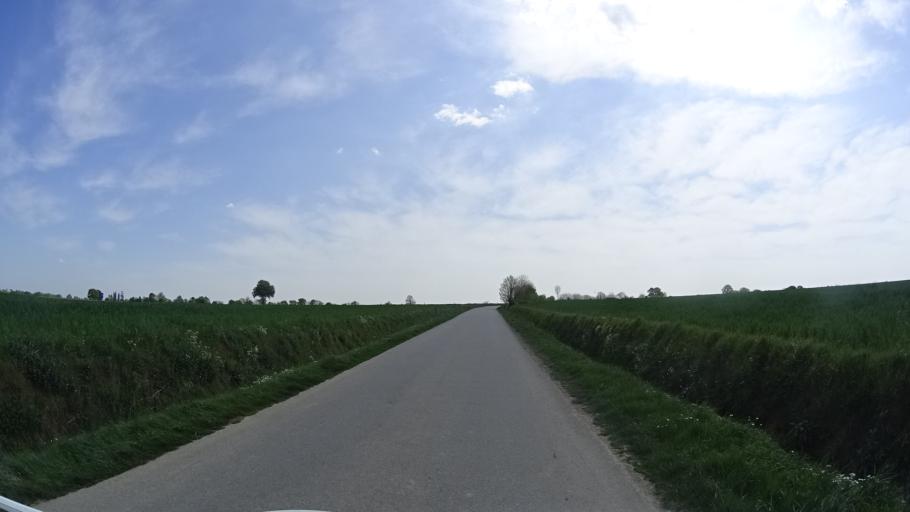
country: FR
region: Brittany
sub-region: Departement d'Ille-et-Vilaine
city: Torce
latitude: 48.0407
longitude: -1.2849
